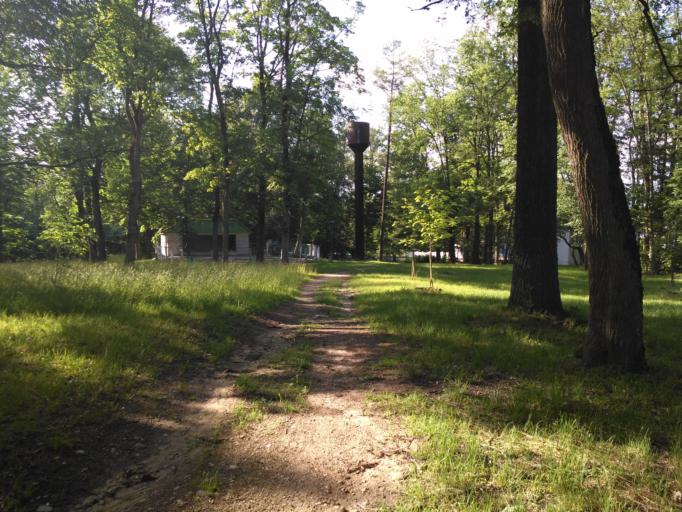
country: BY
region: Minsk
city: Chervyen'
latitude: 53.8847
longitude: 28.6156
